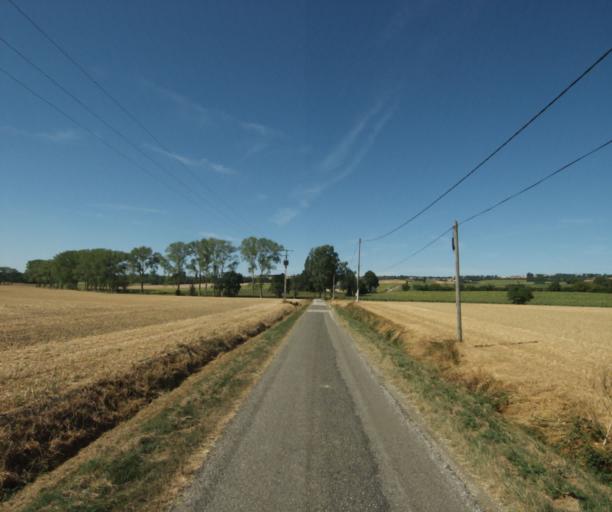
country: FR
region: Midi-Pyrenees
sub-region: Departement de la Haute-Garonne
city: Saint-Felix-Lauragais
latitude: 43.5011
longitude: 1.9015
